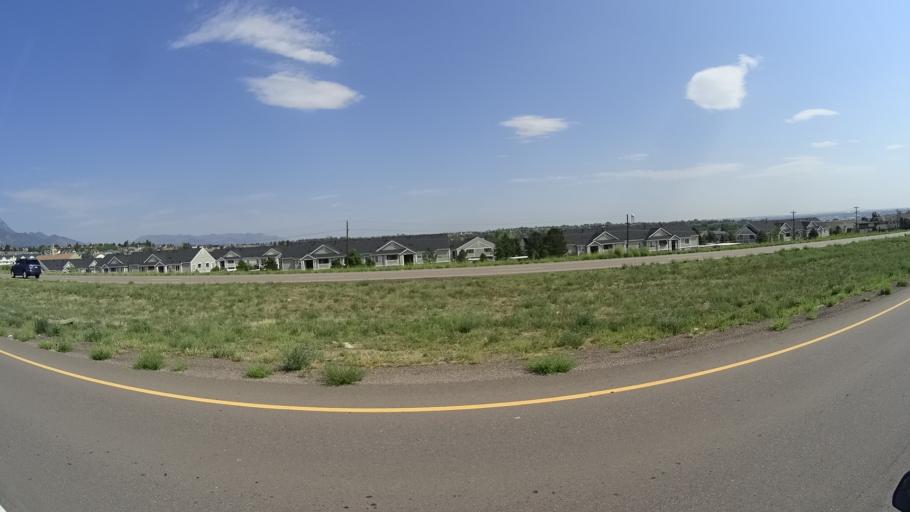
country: US
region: Colorado
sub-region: El Paso County
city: Stratmoor
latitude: 38.7656
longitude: -104.8059
